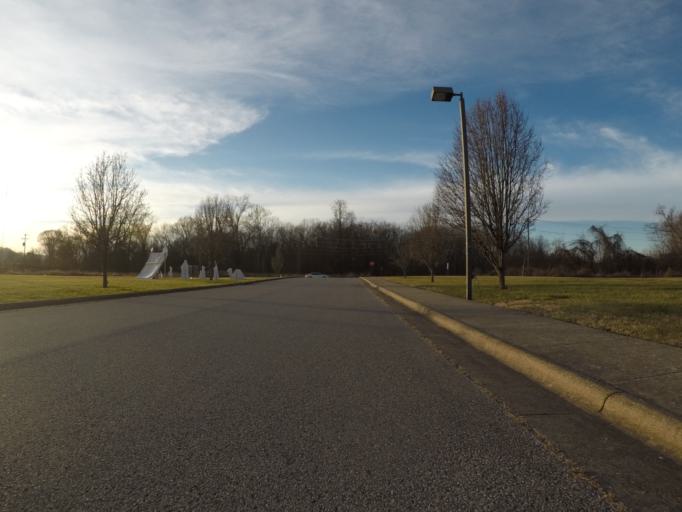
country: US
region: Ohio
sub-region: Lawrence County
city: Burlington
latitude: 38.4031
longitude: -82.4916
